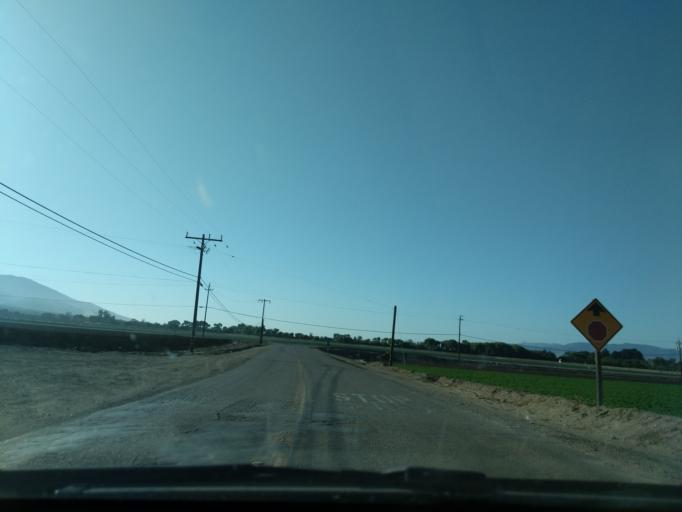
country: US
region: California
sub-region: Monterey County
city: Gonzales
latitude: 36.4720
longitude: -121.4730
